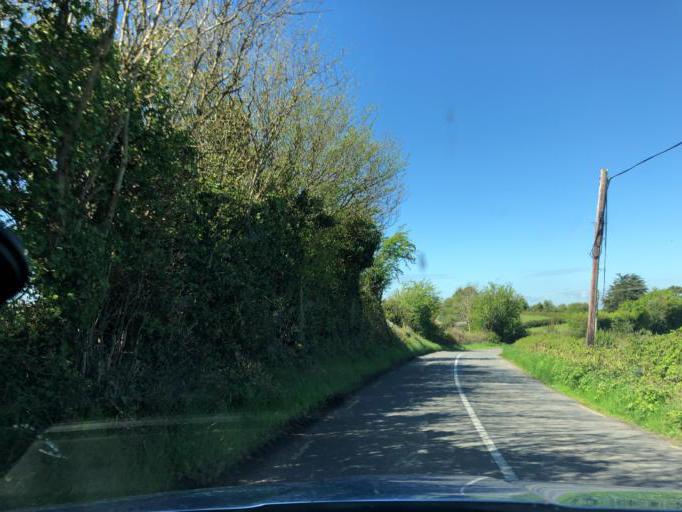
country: IE
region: Connaught
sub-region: County Galway
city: Portumna
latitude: 53.1608
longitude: -8.2706
